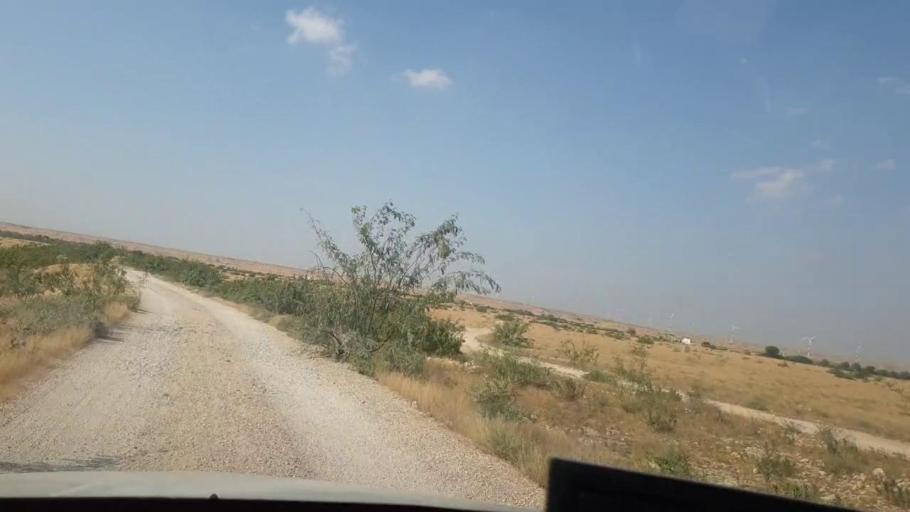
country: PK
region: Sindh
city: Daro Mehar
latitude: 25.0748
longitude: 68.0944
